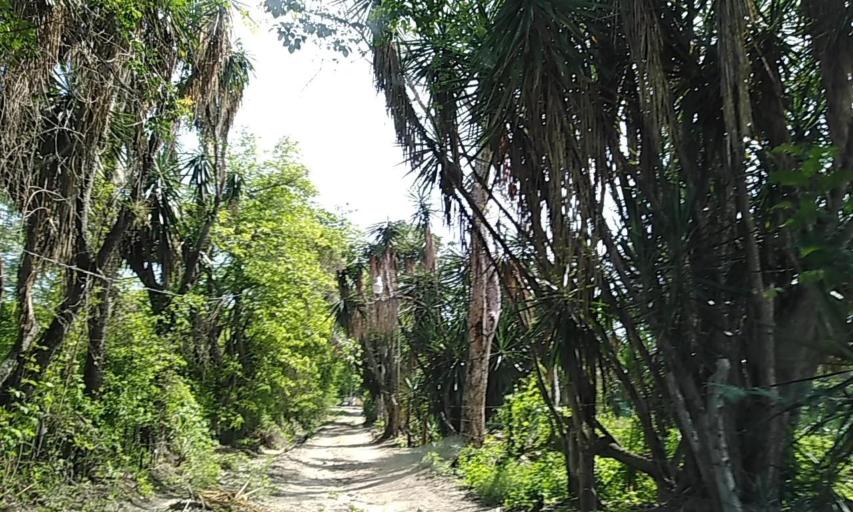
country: MX
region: Veracruz
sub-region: Emiliano Zapata
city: Plan del Rio
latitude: 19.4512
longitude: -96.6800
